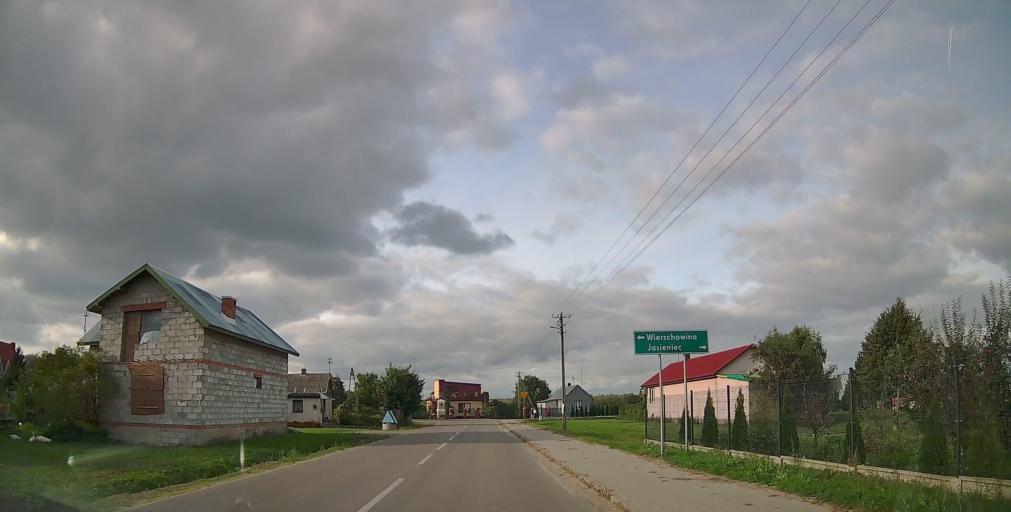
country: PL
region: Masovian Voivodeship
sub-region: Powiat grojecki
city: Jasieniec
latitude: 51.7559
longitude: 20.9611
